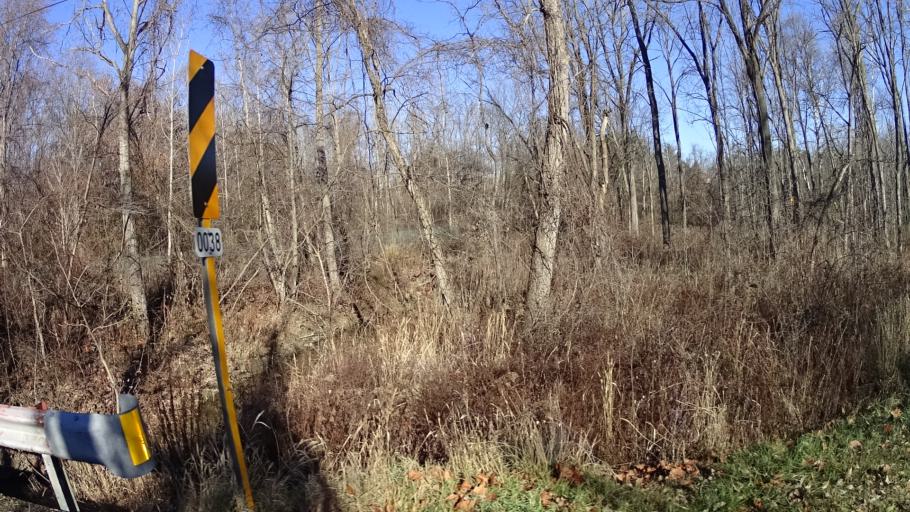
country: US
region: Ohio
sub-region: Huron County
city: New London
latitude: 41.1380
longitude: -82.3320
